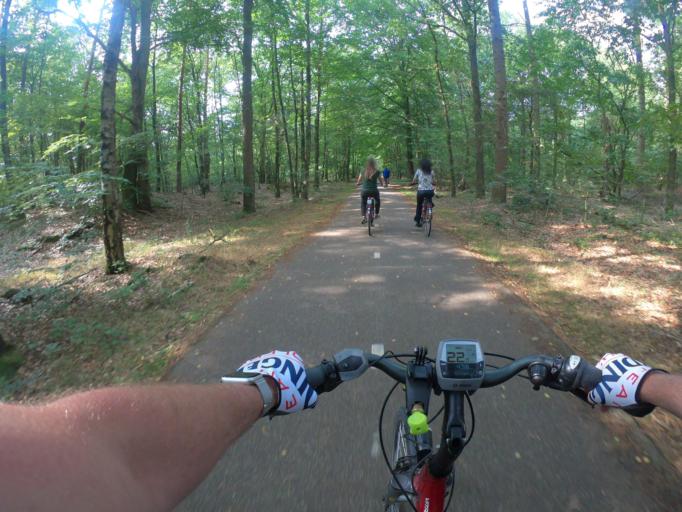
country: NL
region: Gelderland
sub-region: Gemeente Nijmegen
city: Nijmegen
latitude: 51.7983
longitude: 5.8597
